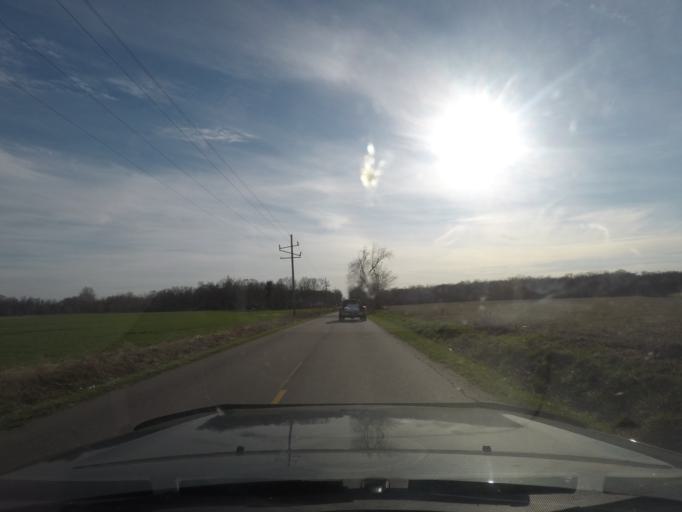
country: US
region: Indiana
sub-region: Marshall County
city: Bremen
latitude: 41.4603
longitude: -86.0818
